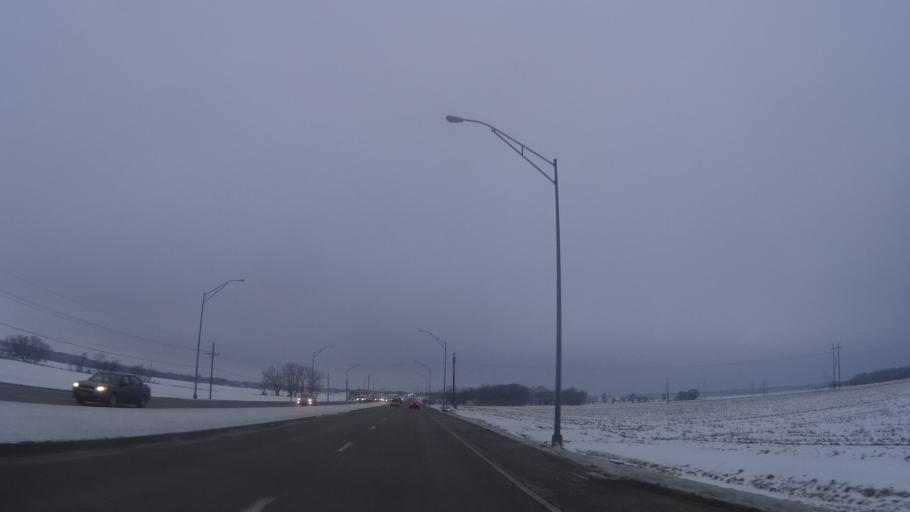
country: US
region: Nebraska
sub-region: Sarpy County
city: La Vista
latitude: 41.1619
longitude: -95.9737
